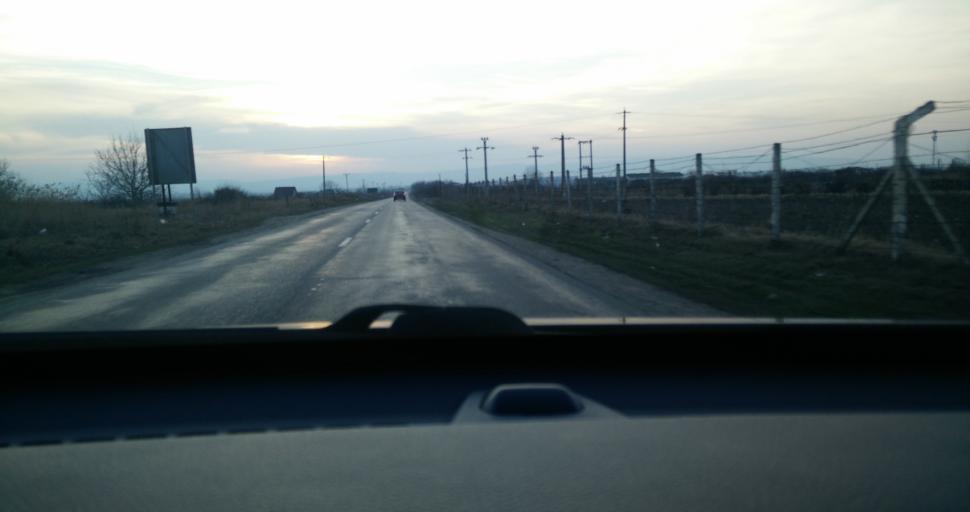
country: RO
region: Vrancea
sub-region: Comuna Milcovul
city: Milcovul
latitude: 45.6797
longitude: 27.2309
